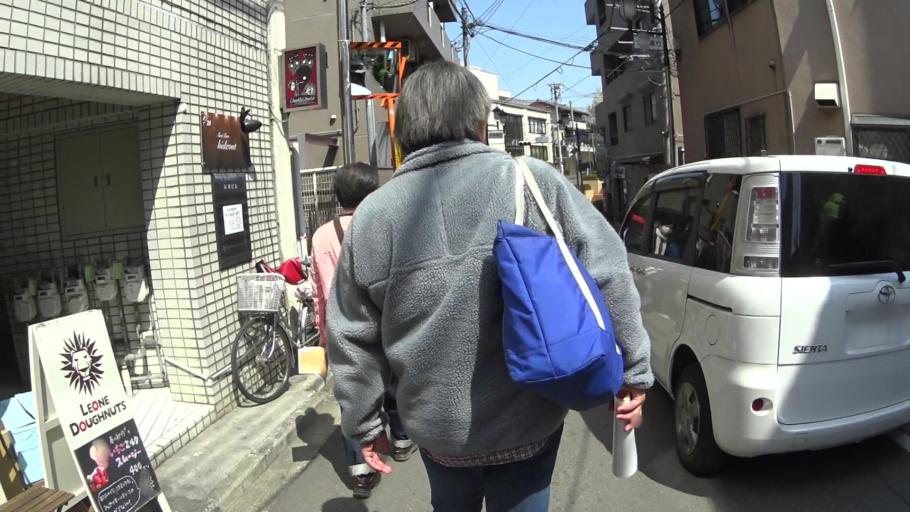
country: JP
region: Tokyo
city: Kokubunji
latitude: 35.7033
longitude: 139.4828
